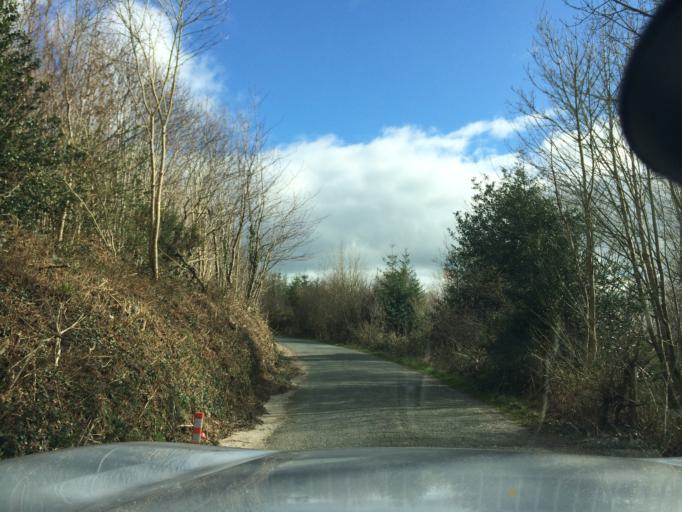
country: IE
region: Munster
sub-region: Waterford
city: Portlaw
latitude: 52.2785
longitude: -7.3692
